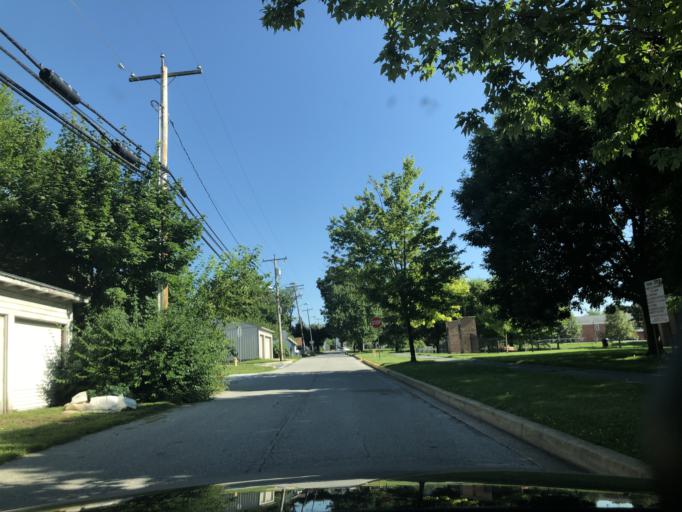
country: US
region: Maryland
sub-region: Carroll County
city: Westminster
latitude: 39.5821
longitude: -76.9981
